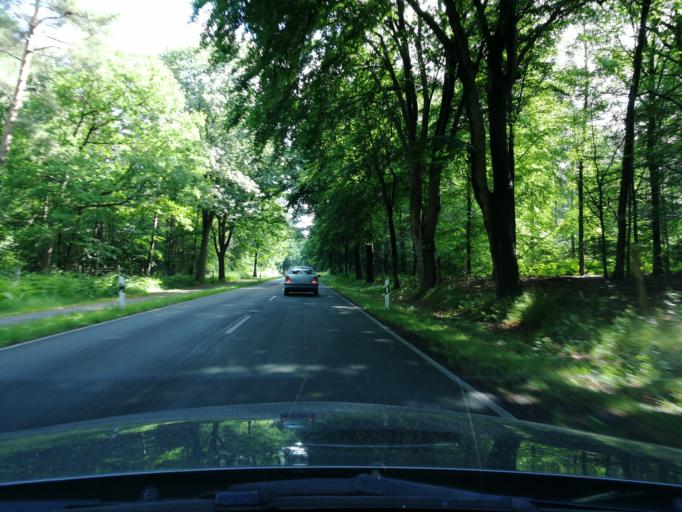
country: DE
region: North Rhine-Westphalia
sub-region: Regierungsbezirk Dusseldorf
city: Kranenburg
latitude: 51.7226
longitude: 6.0557
